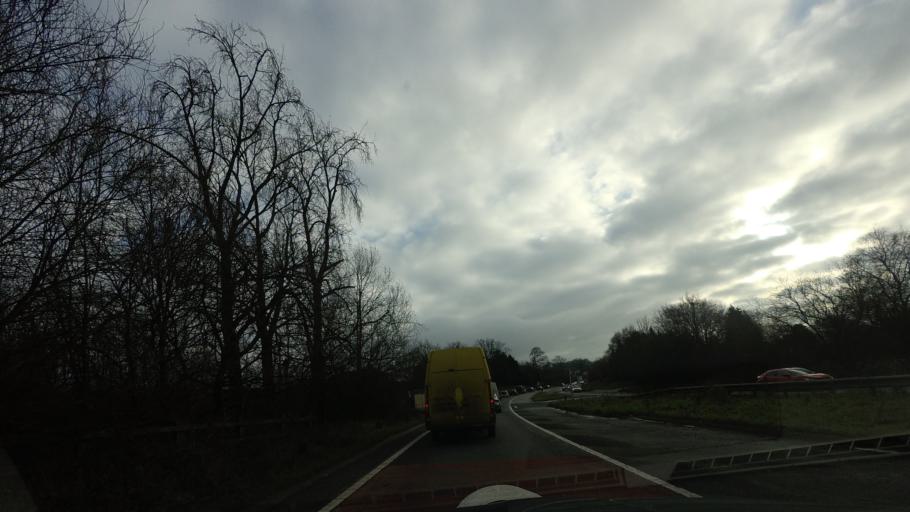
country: GB
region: England
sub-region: Kent
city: Hawkhurst
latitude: 51.0599
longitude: 0.4460
